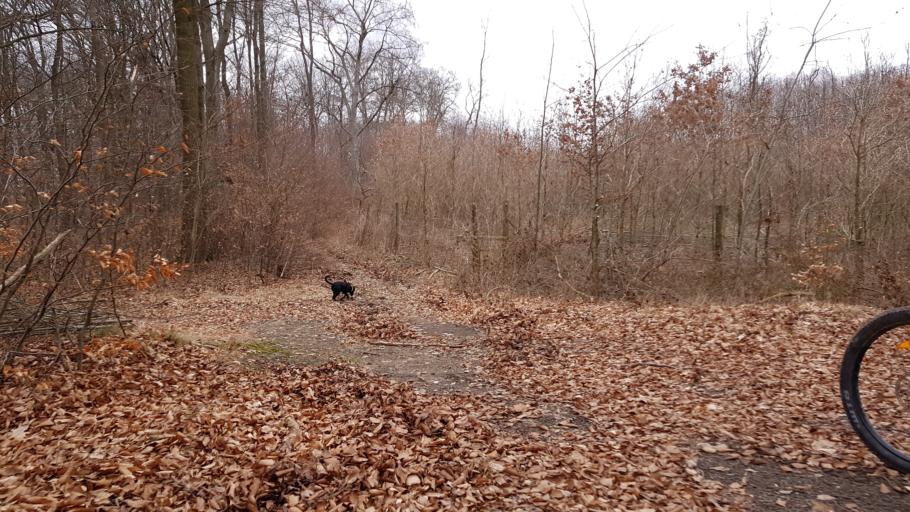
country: PL
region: West Pomeranian Voivodeship
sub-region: Powiat pyrzycki
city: Kozielice
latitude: 53.0703
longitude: 14.7512
